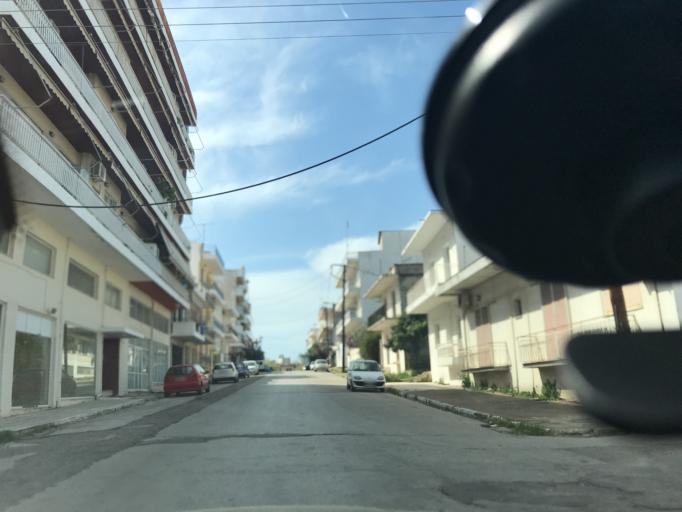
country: GR
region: West Greece
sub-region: Nomos Ileias
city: Pyrgos
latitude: 37.6739
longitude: 21.4468
